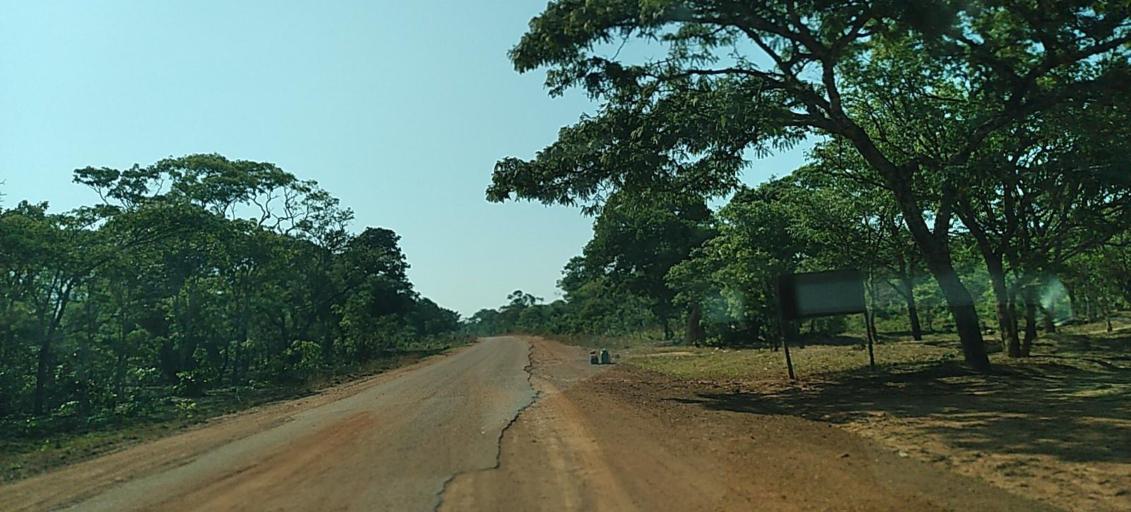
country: ZM
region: North-Western
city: Mwinilunga
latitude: -11.8987
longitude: 25.2755
